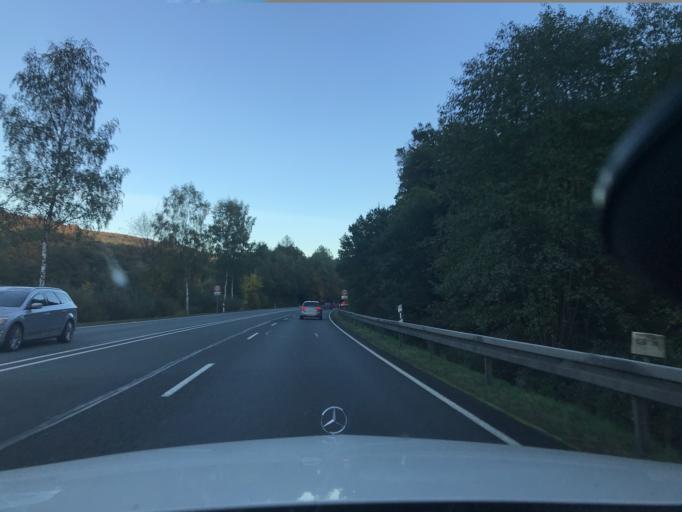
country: DE
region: Hesse
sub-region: Regierungsbezirk Kassel
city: Helsa
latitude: 51.2734
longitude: 9.6585
